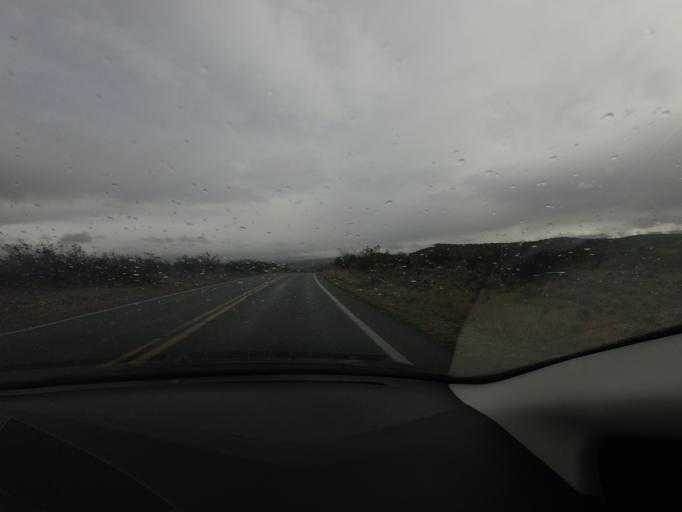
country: US
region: Arizona
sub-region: Yavapai County
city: Lake Montezuma
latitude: 34.6741
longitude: -111.8363
